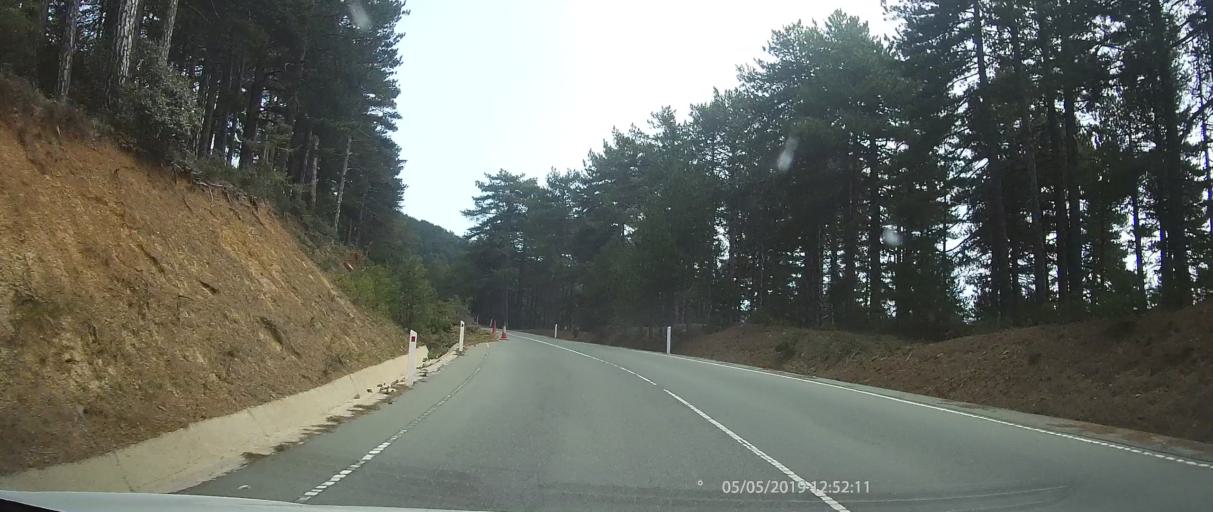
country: CY
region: Lefkosia
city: Kakopetria
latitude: 34.9512
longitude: 32.8359
